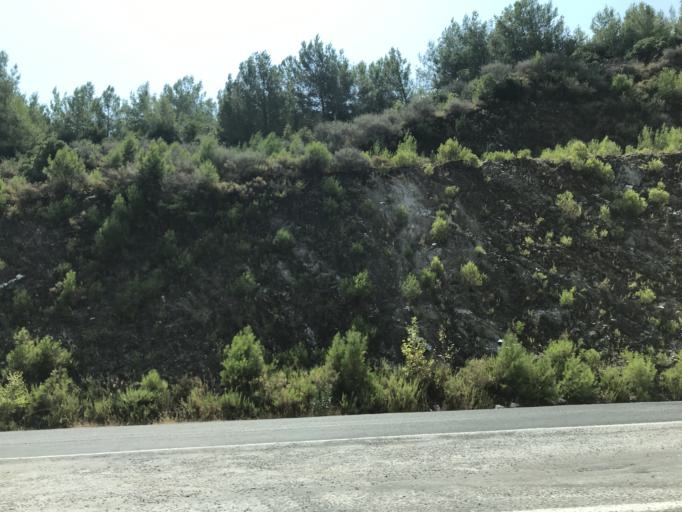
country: TR
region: Mugla
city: Selimiye
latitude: 37.4234
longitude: 27.5691
